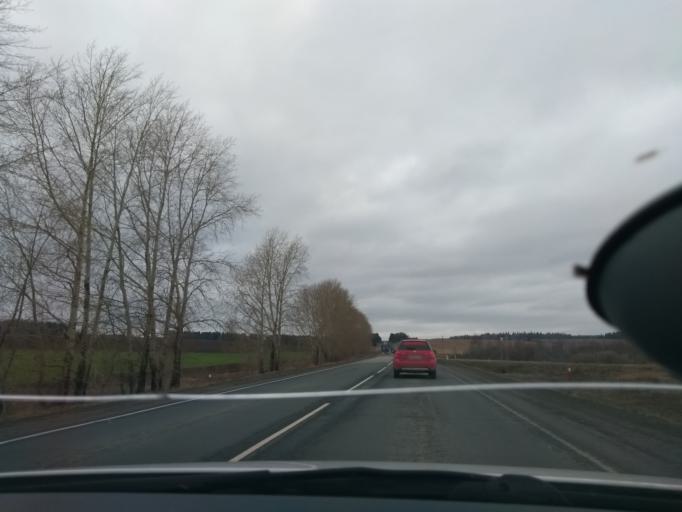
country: RU
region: Perm
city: Kukushtan
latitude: 57.5163
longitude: 56.6382
